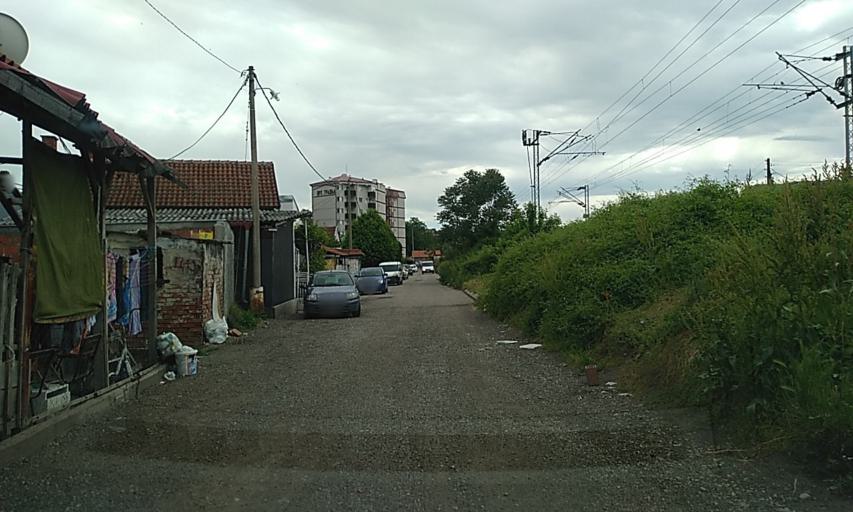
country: RS
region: Central Serbia
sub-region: Nisavski Okrug
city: Nis
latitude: 43.3208
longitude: 21.8870
